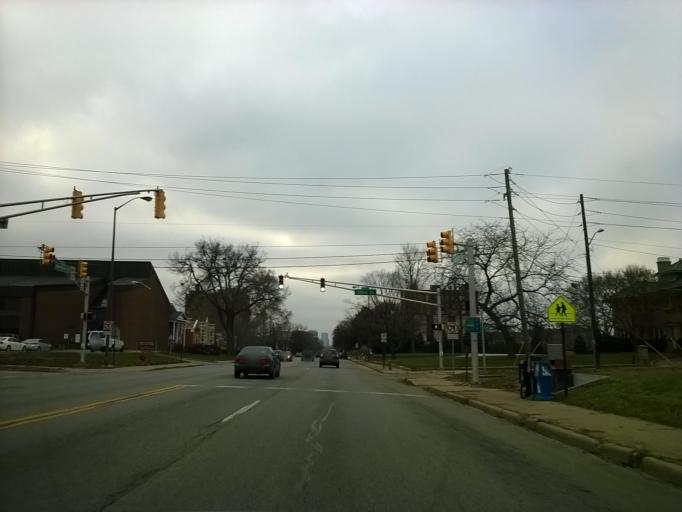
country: US
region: Indiana
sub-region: Marion County
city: Indianapolis
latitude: 39.8142
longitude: -86.1568
